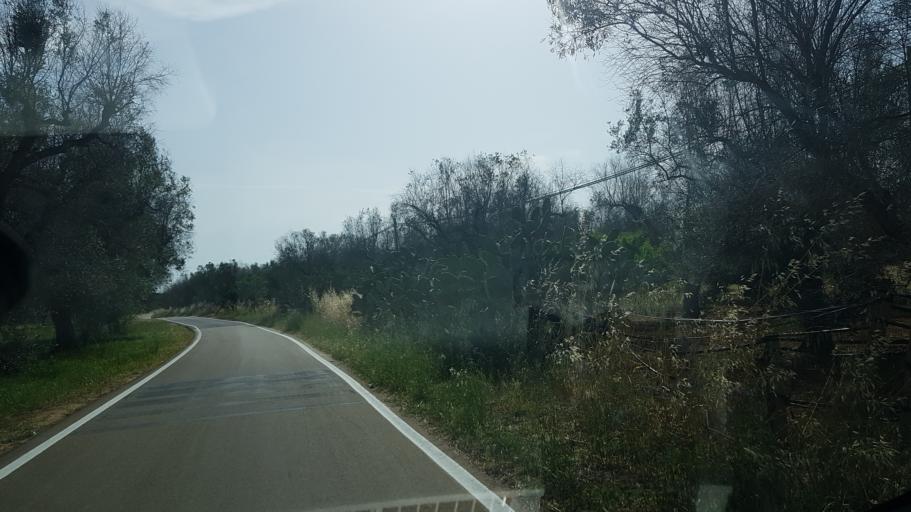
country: IT
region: Apulia
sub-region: Provincia di Brindisi
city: Torchiarolo
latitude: 40.5054
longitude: 18.0655
